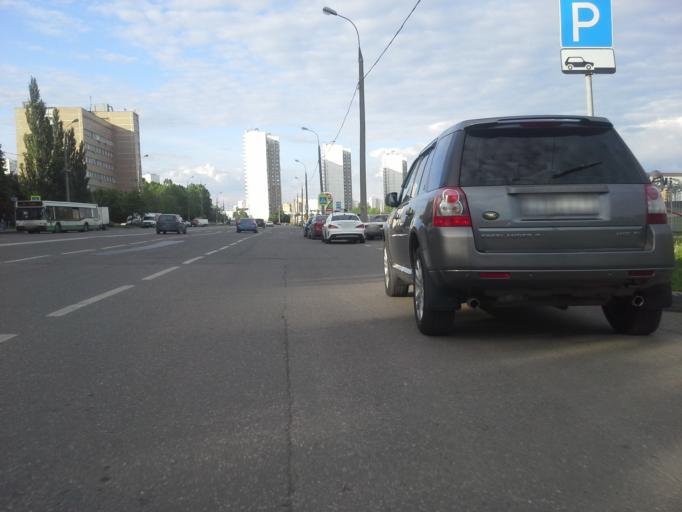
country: RU
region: Moscow
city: Solntsevo
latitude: 55.6369
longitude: 37.3636
